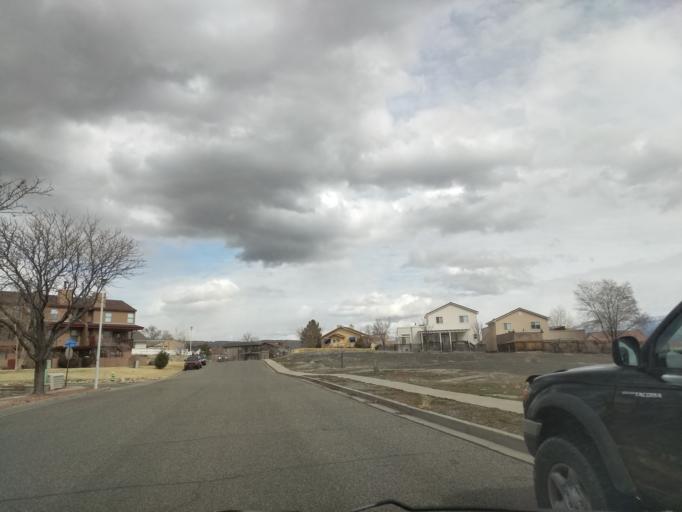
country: US
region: Colorado
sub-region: Mesa County
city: Fruitvale
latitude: 39.0896
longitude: -108.5273
